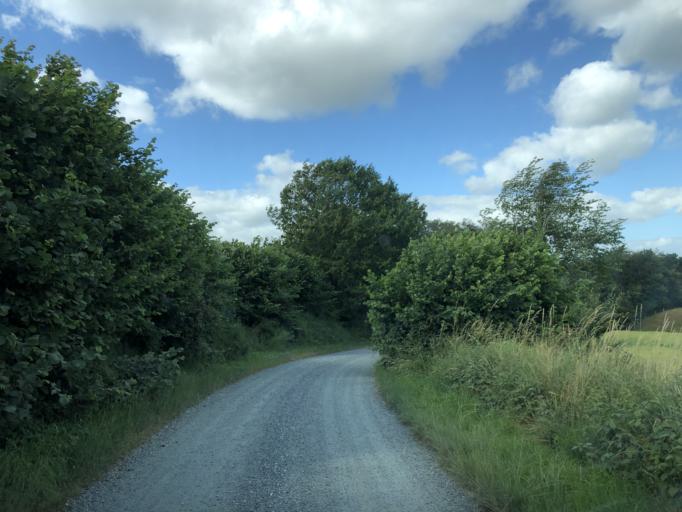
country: DK
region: South Denmark
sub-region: Vejle Kommune
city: Brejning
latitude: 55.6735
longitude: 9.6573
